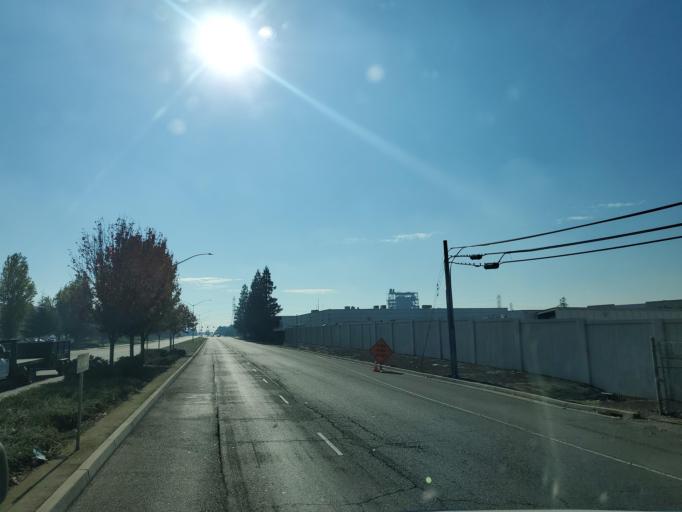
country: US
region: California
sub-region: San Joaquin County
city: Kennedy
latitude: 37.9176
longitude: -121.2612
